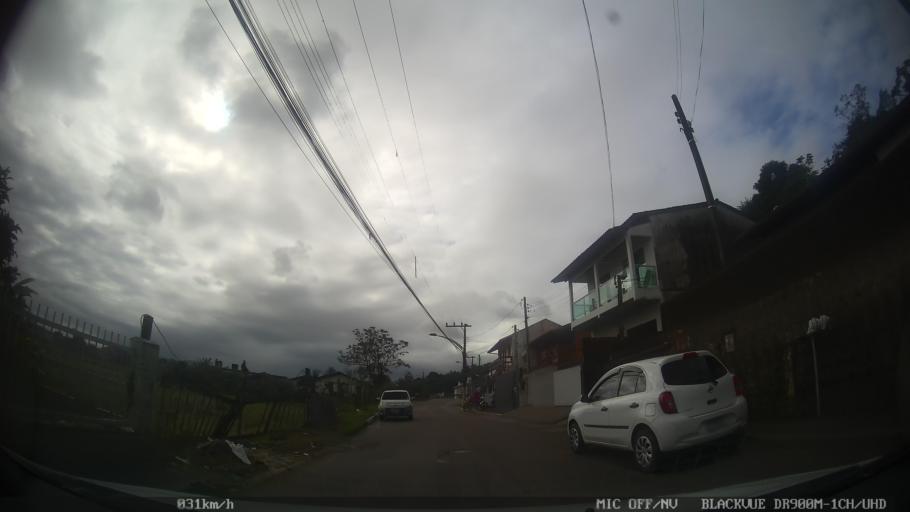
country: BR
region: Santa Catarina
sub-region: Biguacu
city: Biguacu
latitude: -27.5183
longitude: -48.6473
